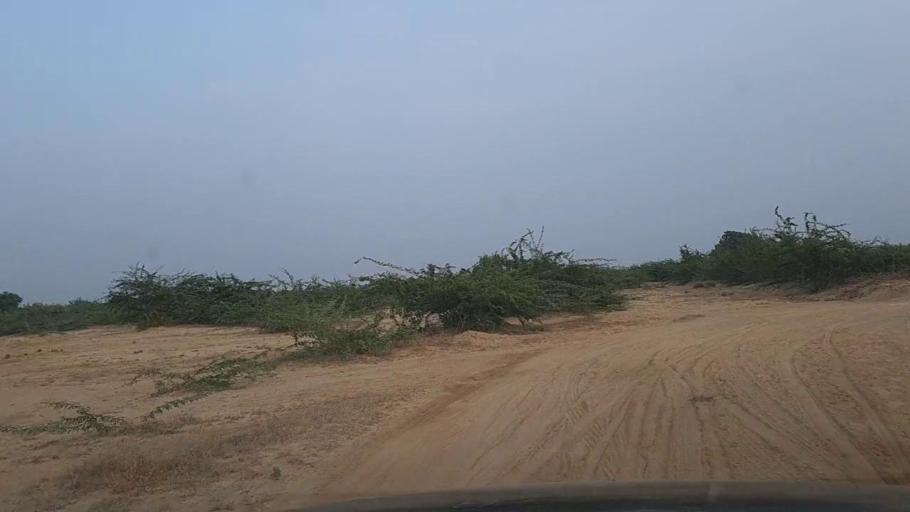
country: PK
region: Sindh
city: Gharo
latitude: 24.7745
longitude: 67.6952
